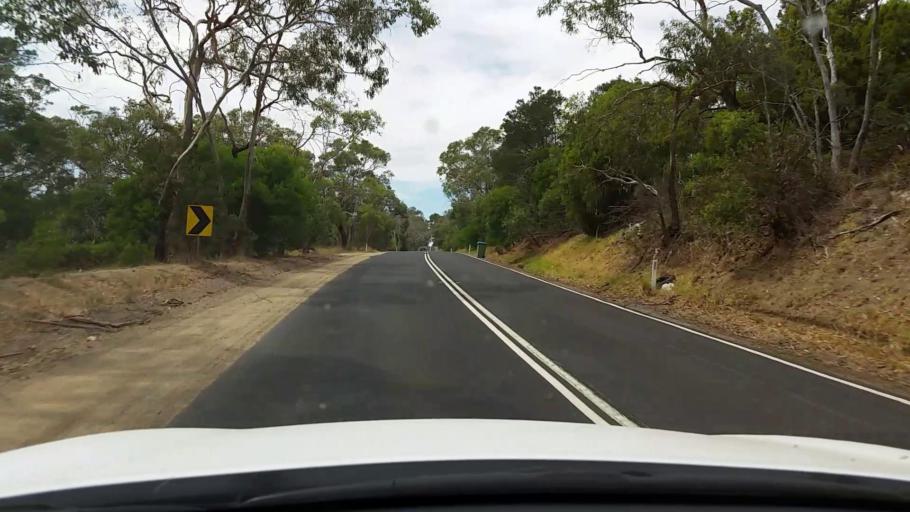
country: AU
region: Victoria
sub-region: Mornington Peninsula
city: Mount Martha
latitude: -38.2958
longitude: 145.0464
